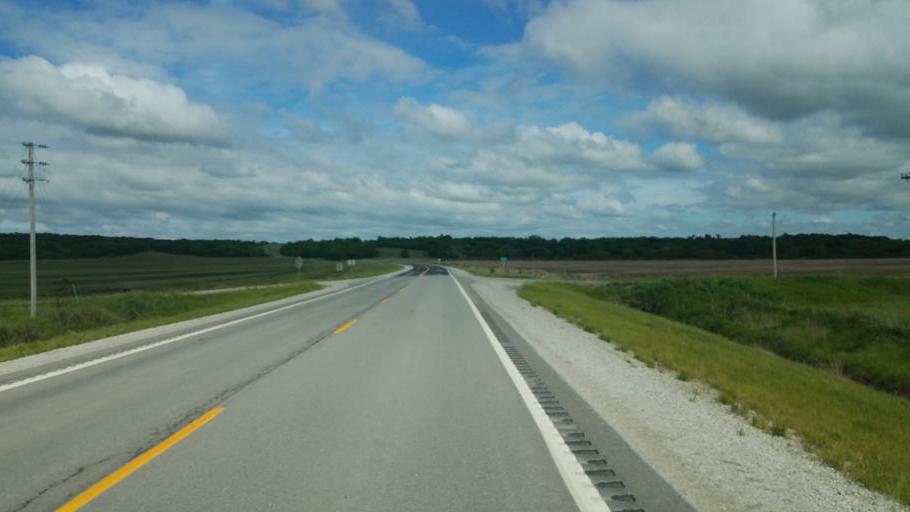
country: US
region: Missouri
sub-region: Mercer County
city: Princeton
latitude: 40.3364
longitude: -93.7644
